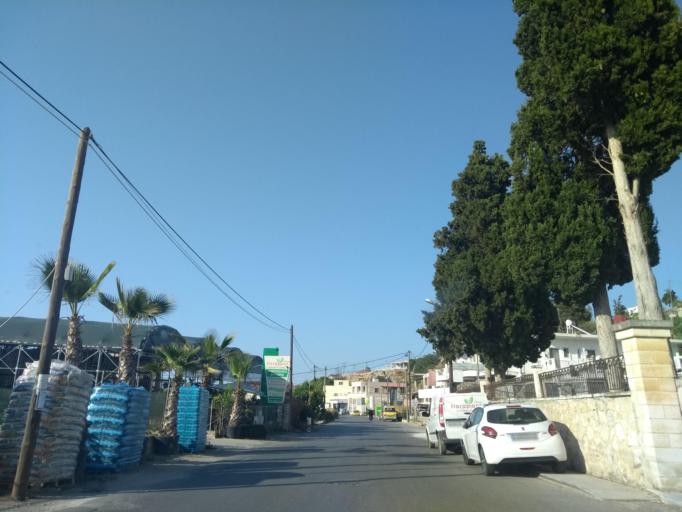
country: GR
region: Crete
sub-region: Nomos Chanias
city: Kalivai
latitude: 35.4468
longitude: 24.1716
